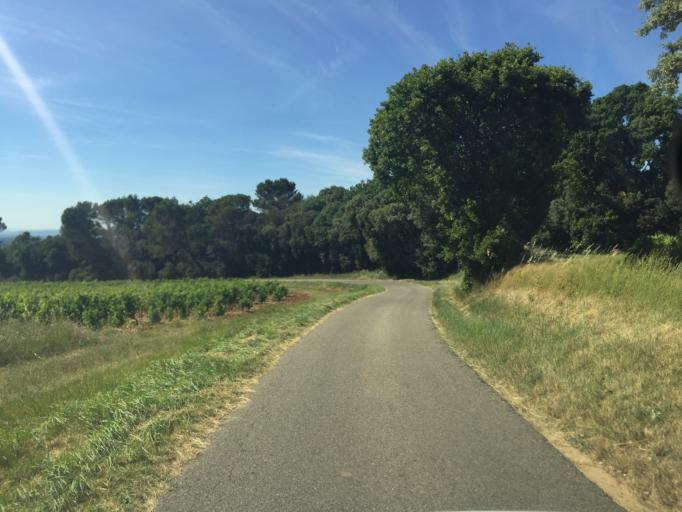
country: FR
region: Provence-Alpes-Cote d'Azur
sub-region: Departement du Vaucluse
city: Chateauneuf-du-Pape
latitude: 44.0838
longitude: 4.8083
